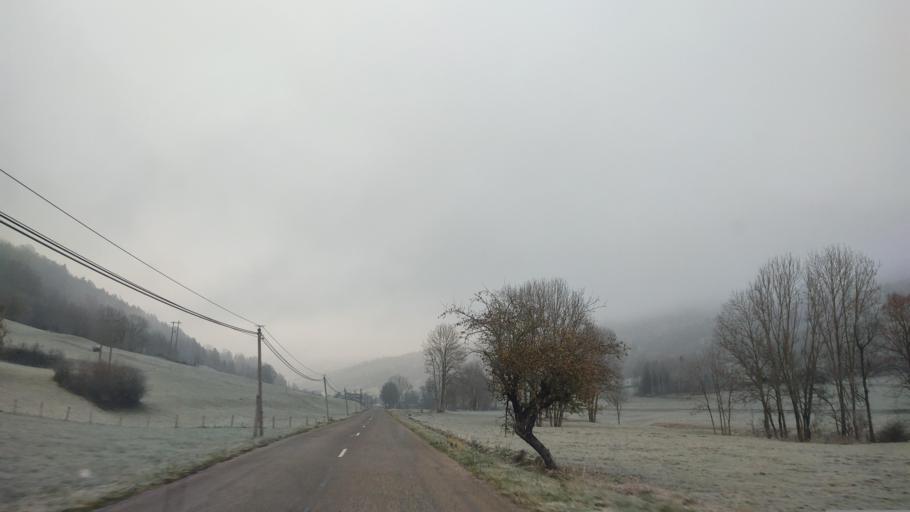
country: FR
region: Rhone-Alpes
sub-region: Departement de la Savoie
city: Coise-Saint-Jean-Pied-Gauthier
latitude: 45.6228
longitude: 6.1471
